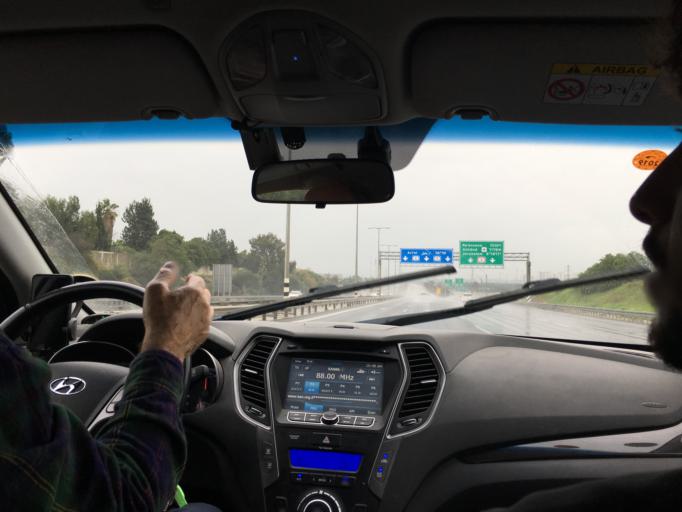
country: IL
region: Tel Aviv
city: Ramat HaSharon
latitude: 32.1275
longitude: 34.8489
